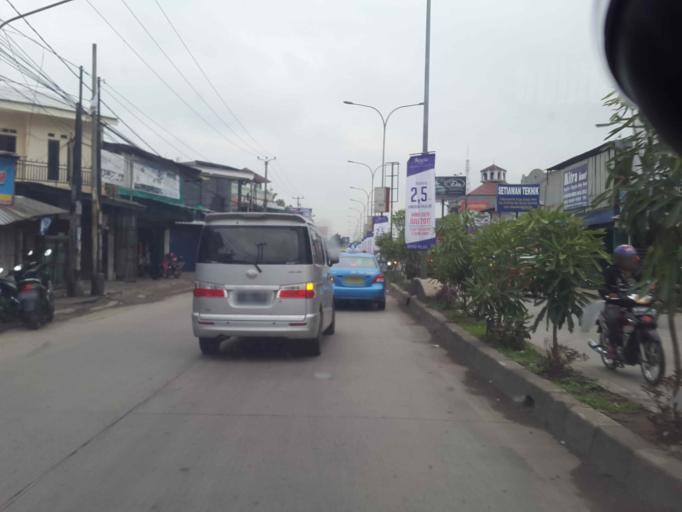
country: ID
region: West Java
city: Cikarang
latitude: -6.3214
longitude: 107.1318
